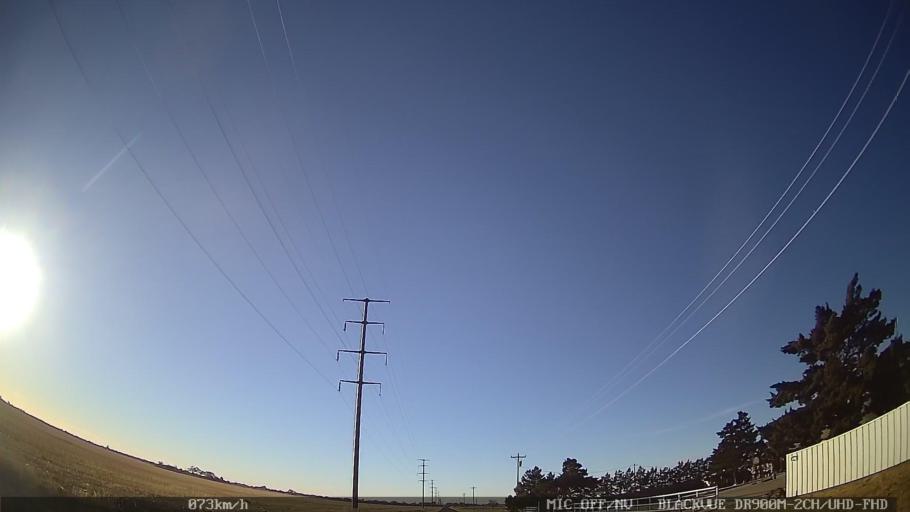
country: US
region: New Mexico
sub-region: Curry County
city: Clovis
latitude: 34.4258
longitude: -103.2493
